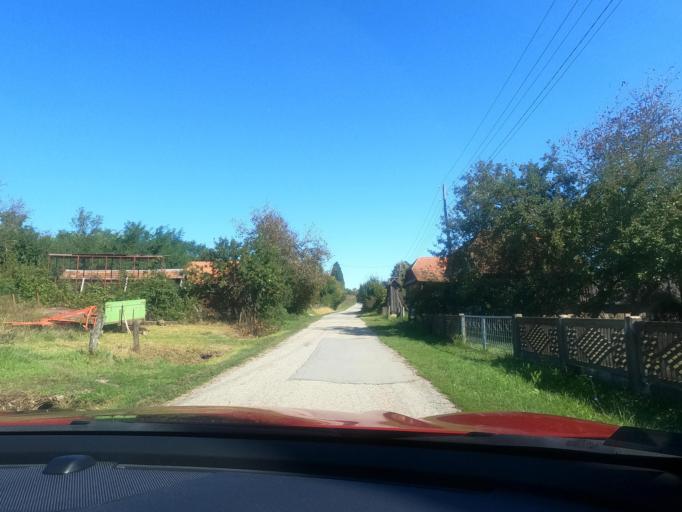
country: HR
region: Sisacko-Moslavacka
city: Petrinja
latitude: 45.3501
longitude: 16.2152
